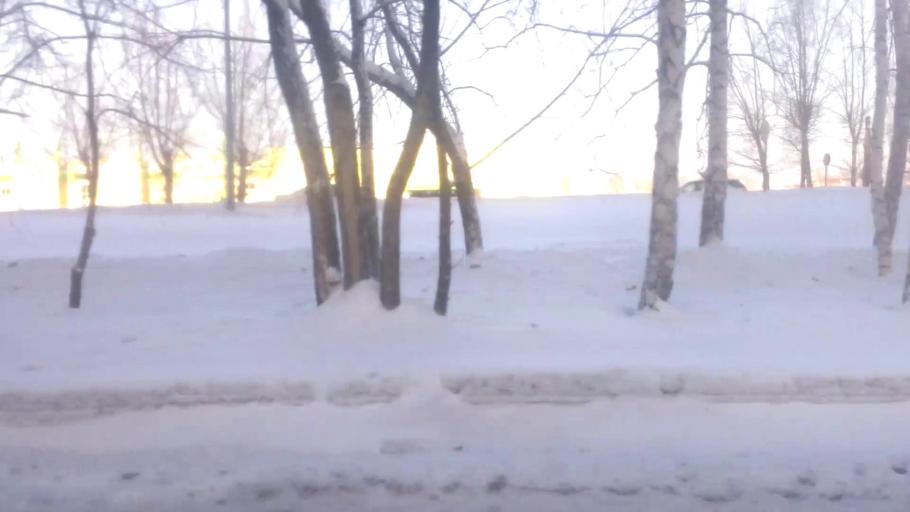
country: RU
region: Altai Krai
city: Novosilikatnyy
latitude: 53.3457
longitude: 83.6552
